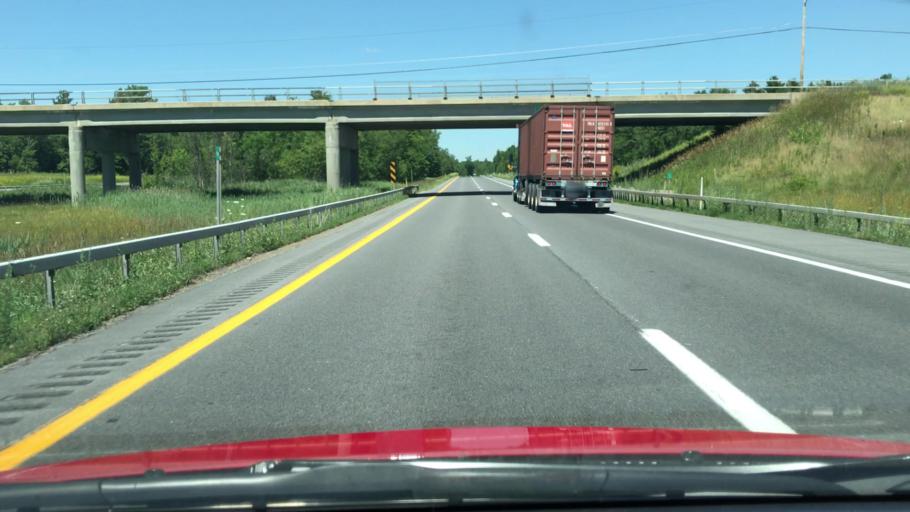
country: US
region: New York
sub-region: Clinton County
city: Champlain
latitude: 44.8892
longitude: -73.4528
